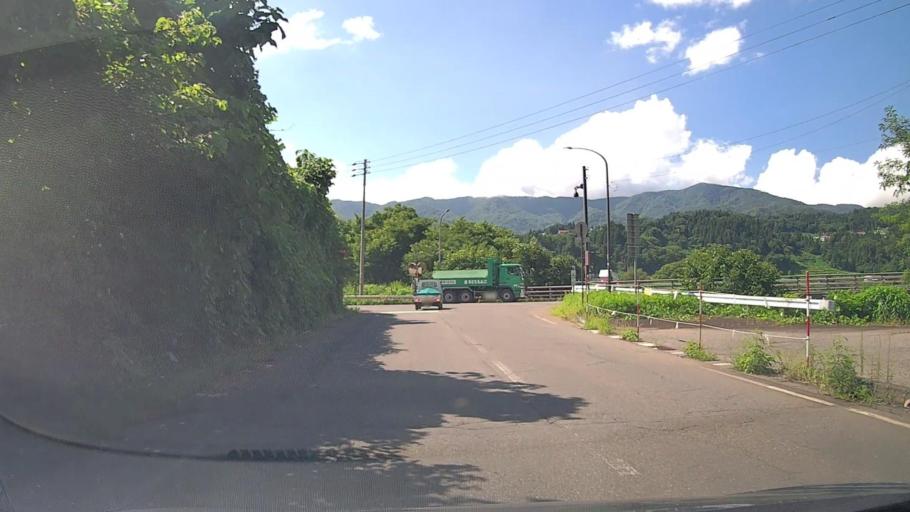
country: JP
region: Nagano
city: Iiyama
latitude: 36.9353
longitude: 138.4230
